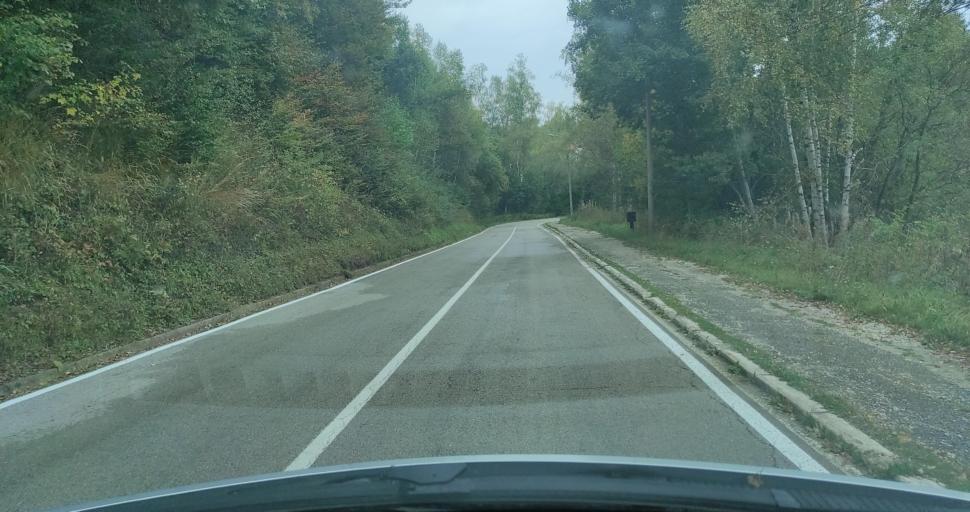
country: RS
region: Central Serbia
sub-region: Jablanicki Okrug
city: Crna Trava
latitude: 42.7451
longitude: 22.3239
